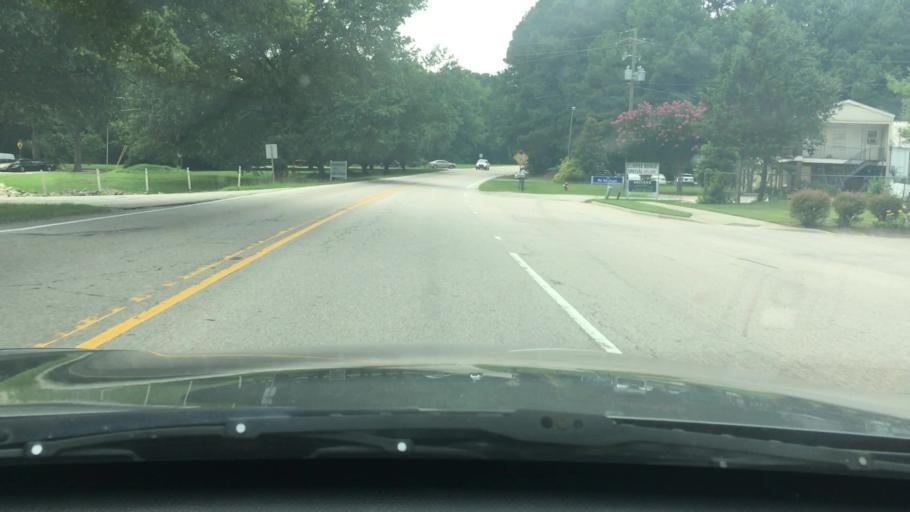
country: US
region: North Carolina
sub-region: Wake County
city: Cary
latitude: 35.7917
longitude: -78.7767
